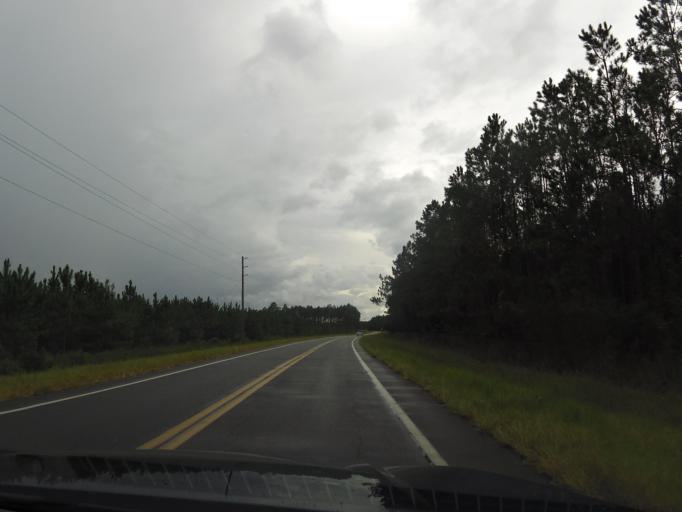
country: US
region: Florida
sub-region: Baker County
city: Macclenny
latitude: 30.3740
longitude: -82.1573
